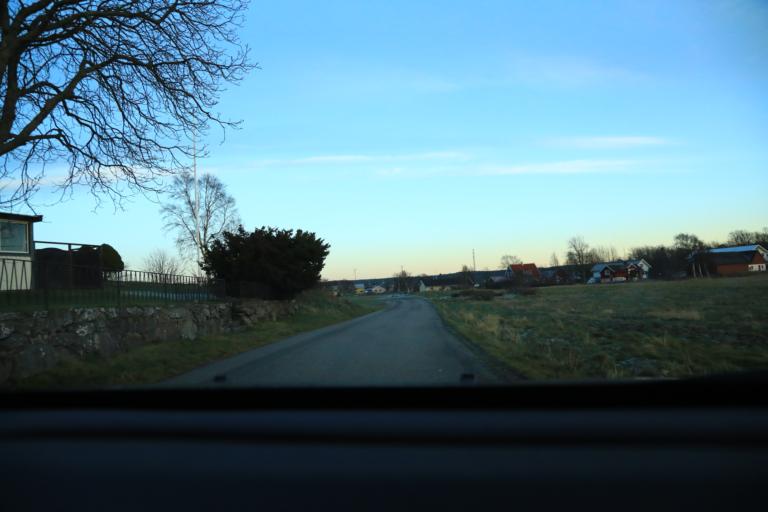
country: SE
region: Halland
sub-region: Varbergs Kommun
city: Varberg
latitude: 57.2013
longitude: 12.1959
